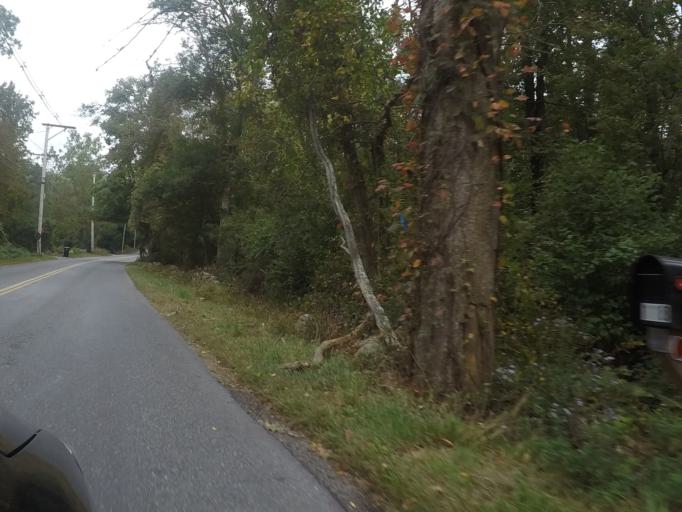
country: US
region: Massachusetts
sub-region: Bristol County
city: Smith Mills
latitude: 41.5649
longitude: -71.0068
